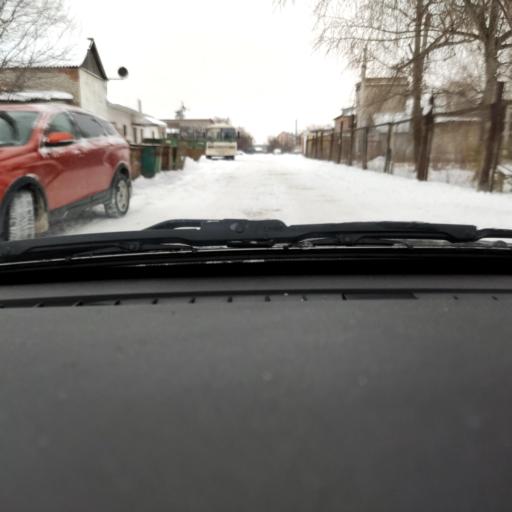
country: RU
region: Voronezj
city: Novaya Usman'
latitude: 51.6452
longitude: 39.4177
